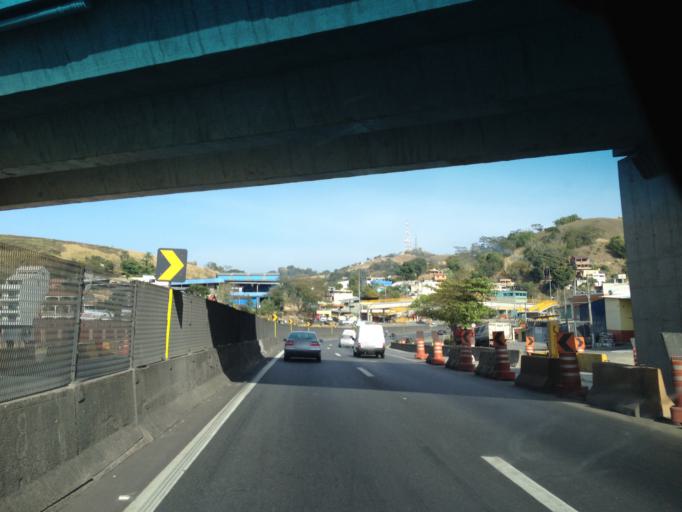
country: BR
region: Rio de Janeiro
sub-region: Barra Mansa
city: Barra Mansa
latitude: -22.5625
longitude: -44.1681
